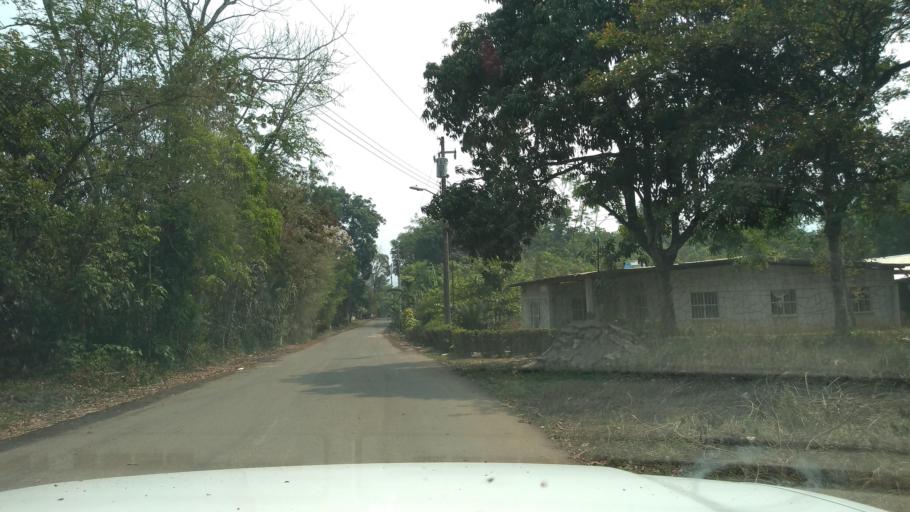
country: MX
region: Veracruz
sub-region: Tezonapa
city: Laguna Chica (Pueblo Nuevo)
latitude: 18.5377
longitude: -96.7843
